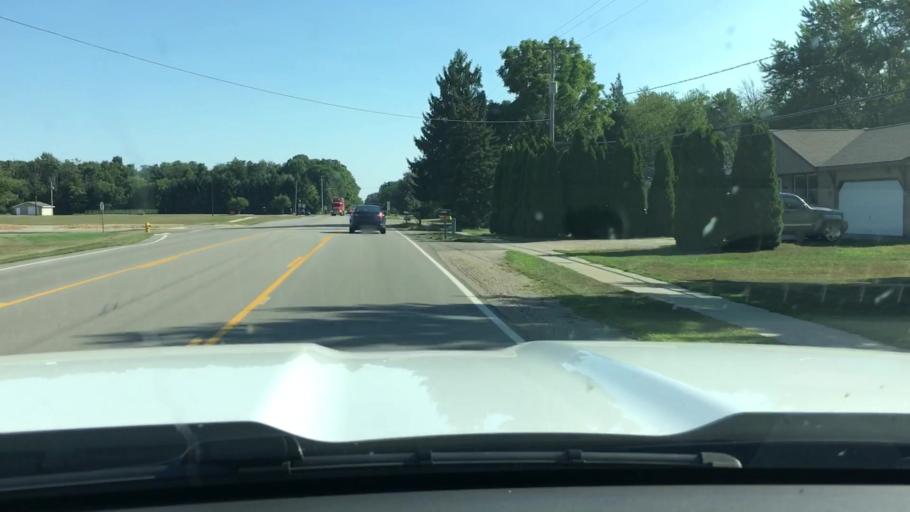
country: US
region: Michigan
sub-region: Ottawa County
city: Allendale
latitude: 42.9649
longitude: -85.9538
